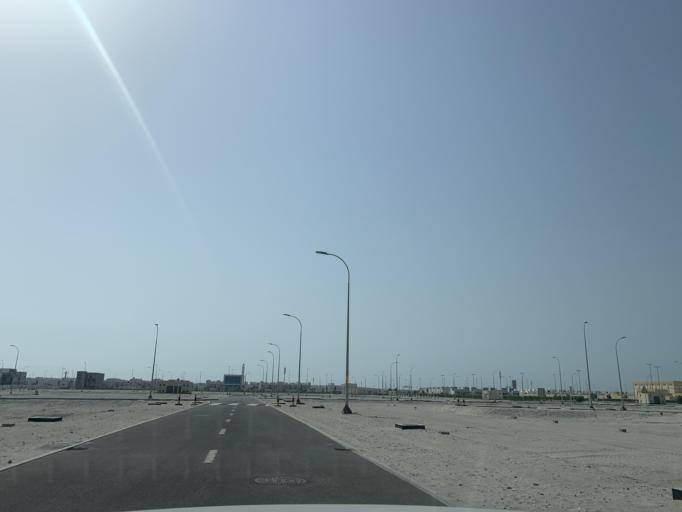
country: BH
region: Muharraq
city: Al Muharraq
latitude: 26.3064
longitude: 50.6340
